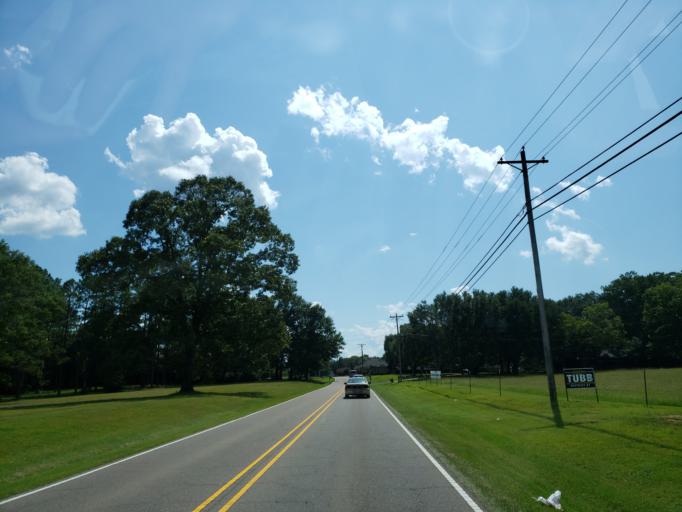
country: US
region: Mississippi
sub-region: Lamar County
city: West Hattiesburg
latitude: 31.2975
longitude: -89.3850
